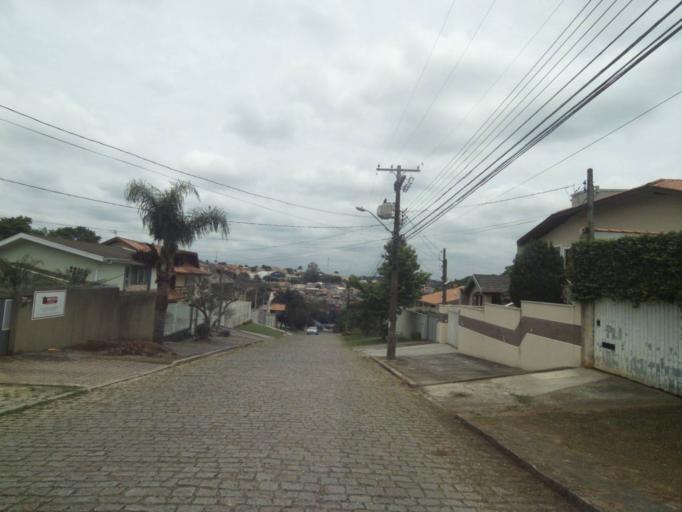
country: BR
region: Parana
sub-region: Curitiba
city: Curitiba
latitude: -25.3847
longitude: -49.2916
